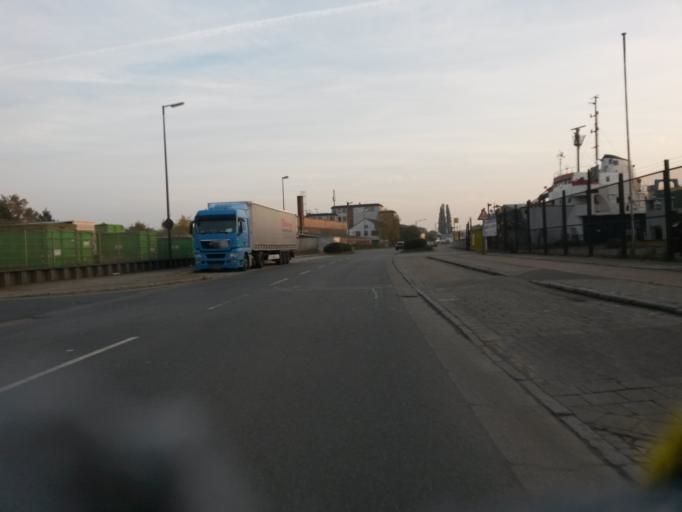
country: DE
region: Bremen
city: Bremen
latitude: 53.0531
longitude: 8.8822
